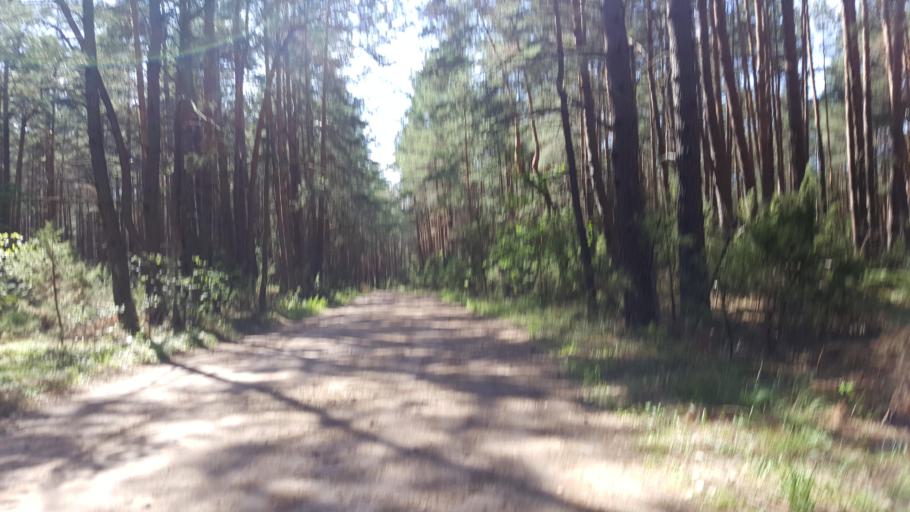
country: BY
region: Brest
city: Zhabinka
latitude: 52.4602
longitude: 24.1329
